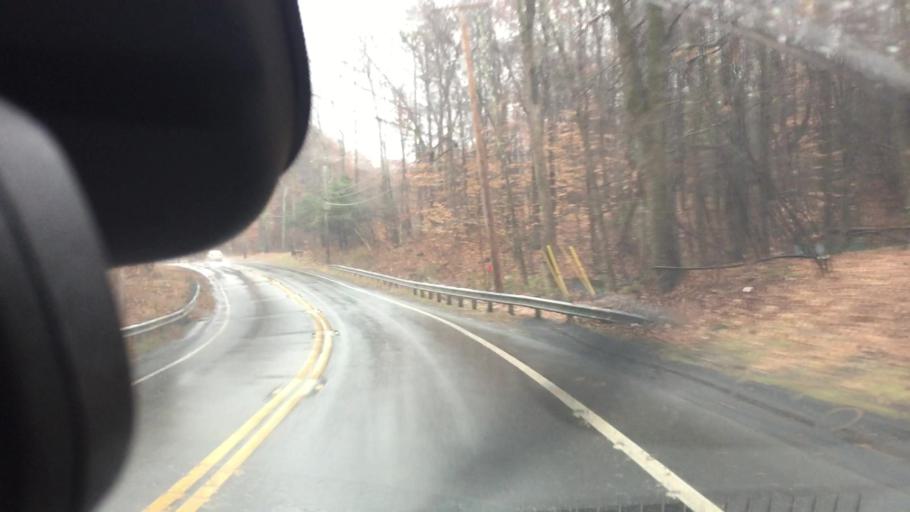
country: US
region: Massachusetts
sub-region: Hampden County
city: Granville
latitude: 42.1722
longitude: -72.9100
